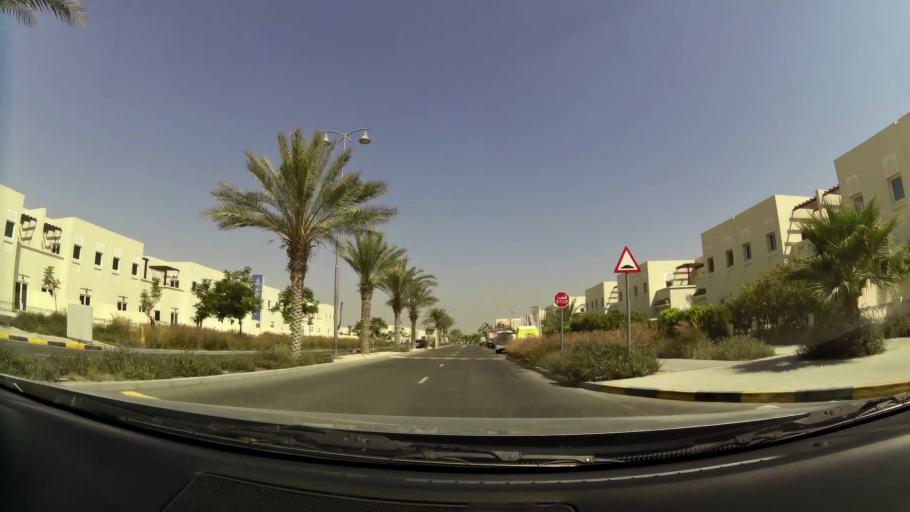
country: AE
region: Dubai
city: Dubai
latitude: 25.0269
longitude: 55.1527
